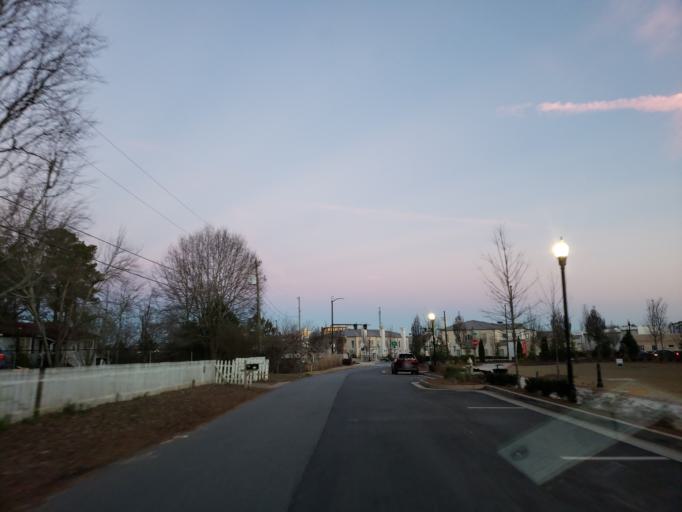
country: US
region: Georgia
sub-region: Fulton County
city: Alpharetta
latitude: 34.0712
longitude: -84.2832
